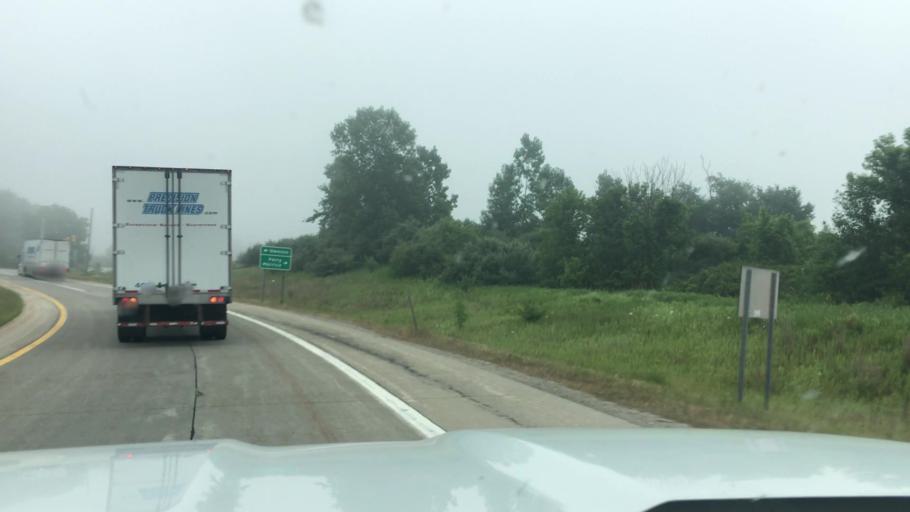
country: US
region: Michigan
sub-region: Shiawassee County
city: Perry
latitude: 42.8375
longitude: -84.2216
